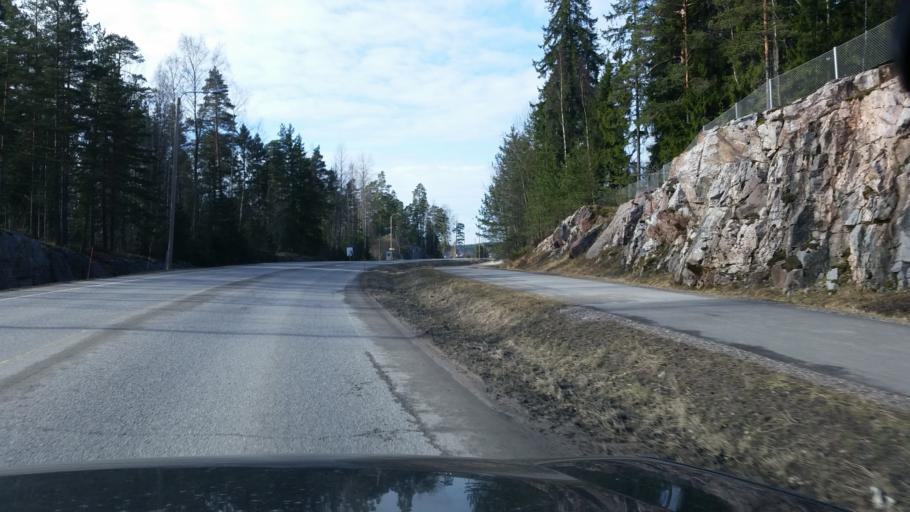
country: FI
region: Uusimaa
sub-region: Helsinki
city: Kirkkonummi
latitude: 60.1106
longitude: 24.4453
